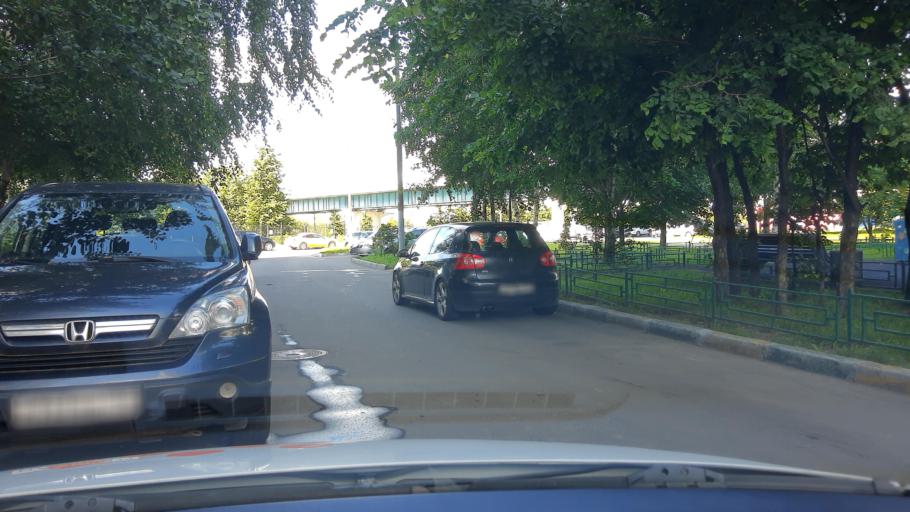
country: RU
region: Moskovskaya
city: Shcherbinka
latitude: 55.5435
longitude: 37.5391
